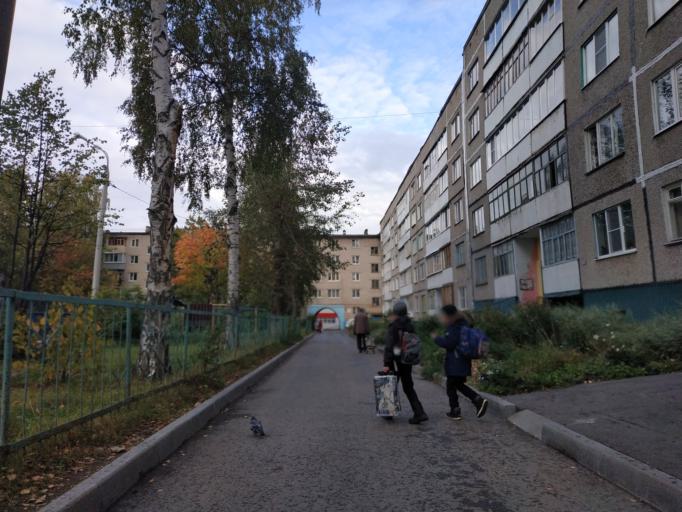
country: RU
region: Chuvashia
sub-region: Cheboksarskiy Rayon
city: Cheboksary
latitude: 56.1422
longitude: 47.1885
